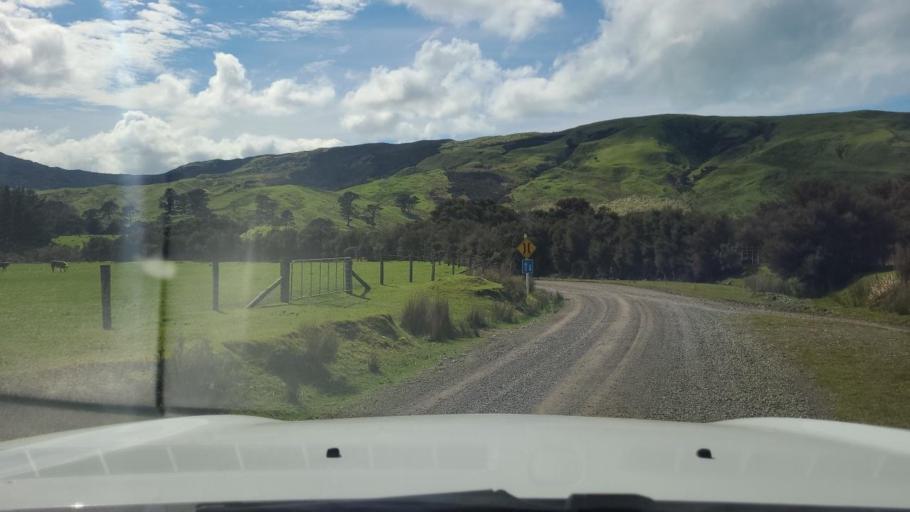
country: NZ
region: Wellington
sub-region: South Wairarapa District
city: Waipawa
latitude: -41.3779
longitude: 175.7232
